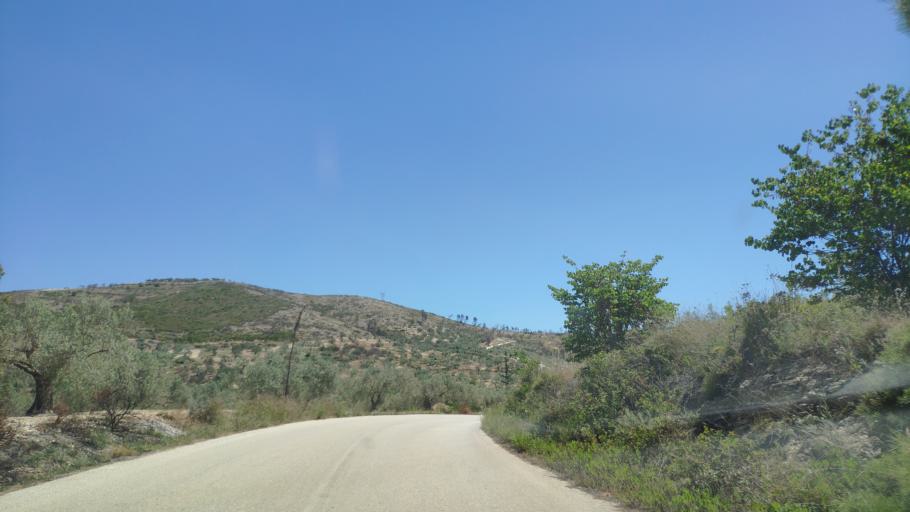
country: GR
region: Peloponnese
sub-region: Nomos Korinthias
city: Athikia
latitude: 37.8351
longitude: 22.9325
